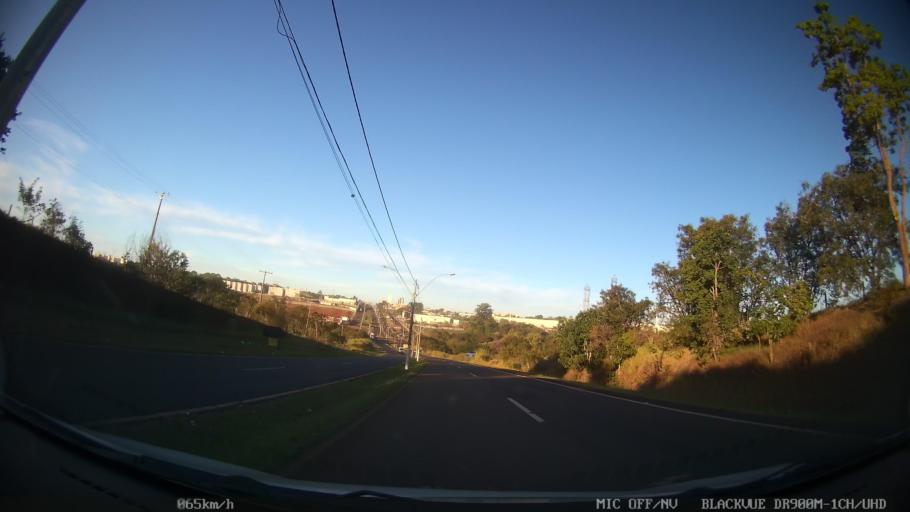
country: BR
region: Sao Paulo
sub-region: Araraquara
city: Araraquara
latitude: -21.7882
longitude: -48.2143
